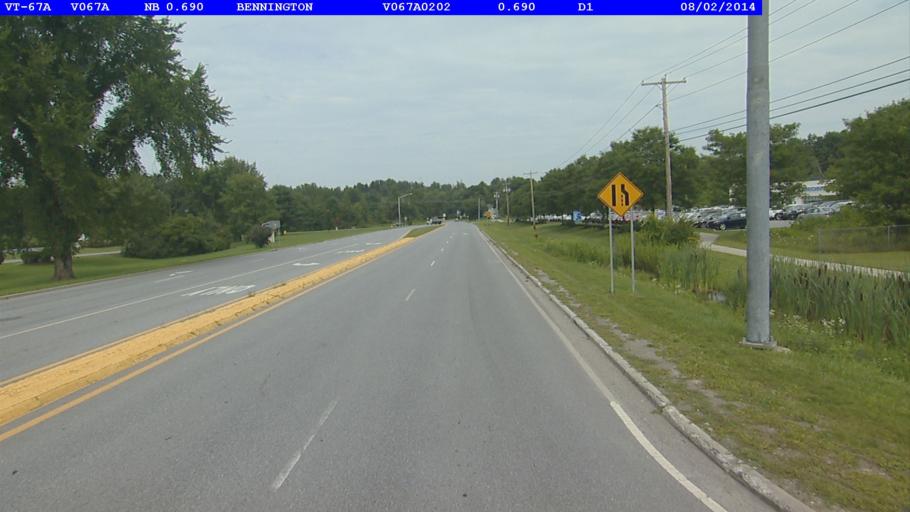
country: US
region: Vermont
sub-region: Bennington County
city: North Bennington
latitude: 42.9084
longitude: -73.2205
